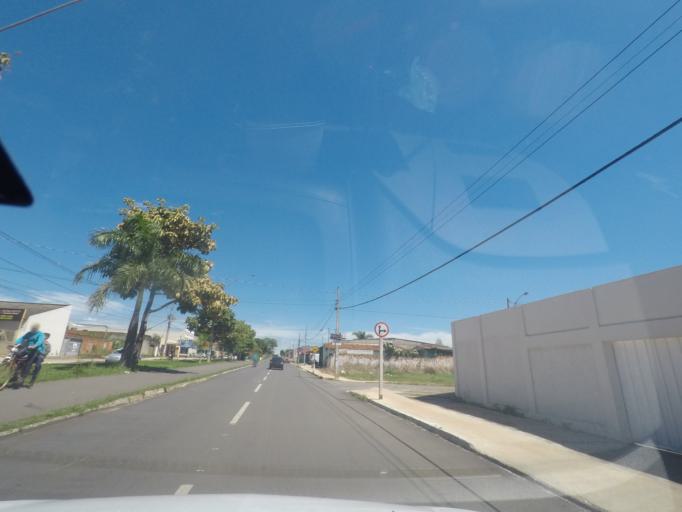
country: BR
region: Goias
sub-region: Aparecida De Goiania
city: Aparecida de Goiania
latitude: -16.7720
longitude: -49.3409
